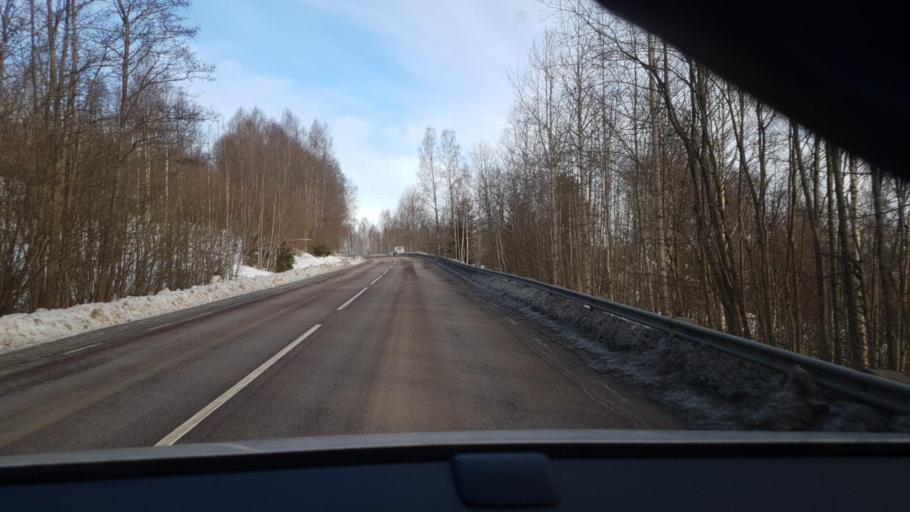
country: SE
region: Vaermland
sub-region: Eda Kommun
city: Amotfors
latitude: 59.6935
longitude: 12.3436
